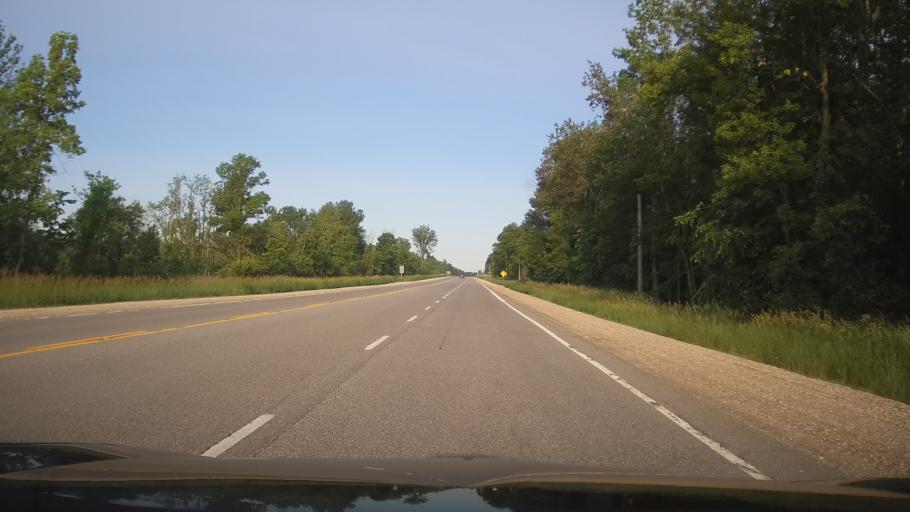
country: CA
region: Ontario
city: Perth
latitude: 44.8736
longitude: -76.3640
